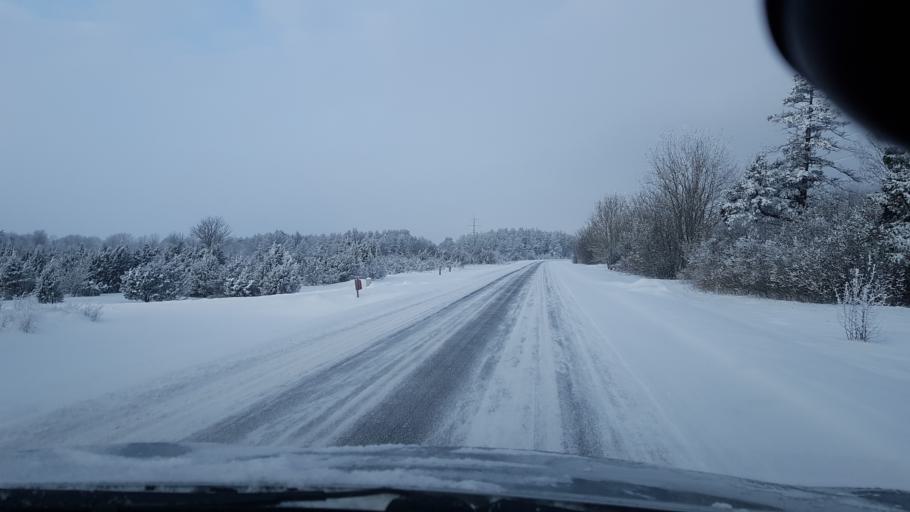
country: EE
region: Harju
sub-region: Keila linn
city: Keila
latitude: 59.3480
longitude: 24.4305
